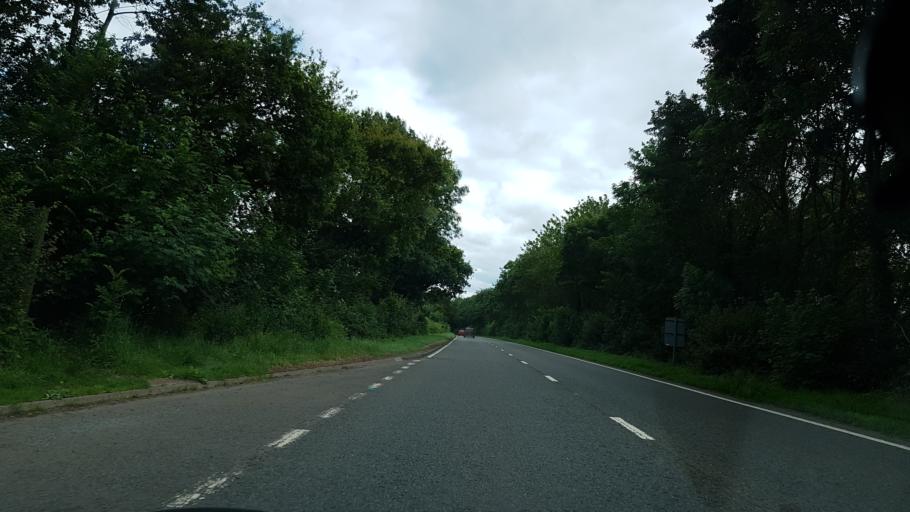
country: GB
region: Wales
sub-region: Monmouthshire
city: Abergavenny
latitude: 51.8158
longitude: -3.0082
